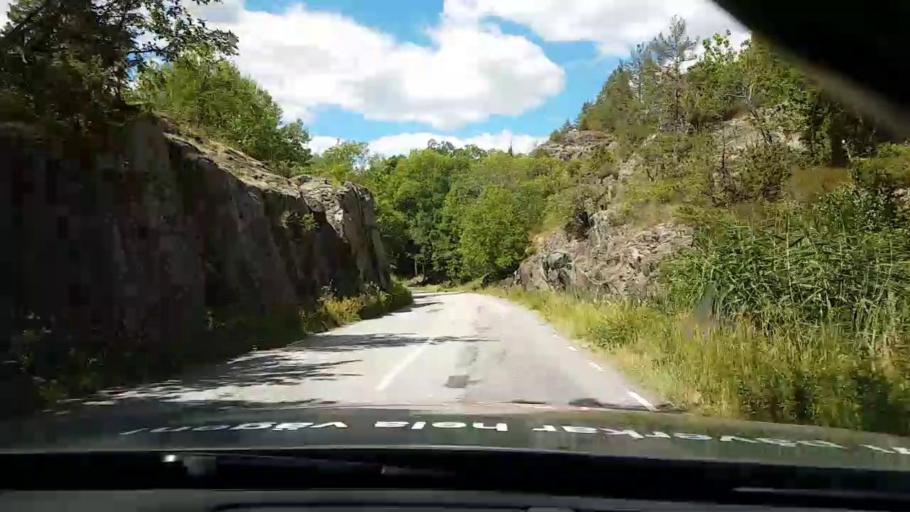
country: SE
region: Kalmar
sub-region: Vasterviks Kommun
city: Overum
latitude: 58.0711
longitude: 16.3800
